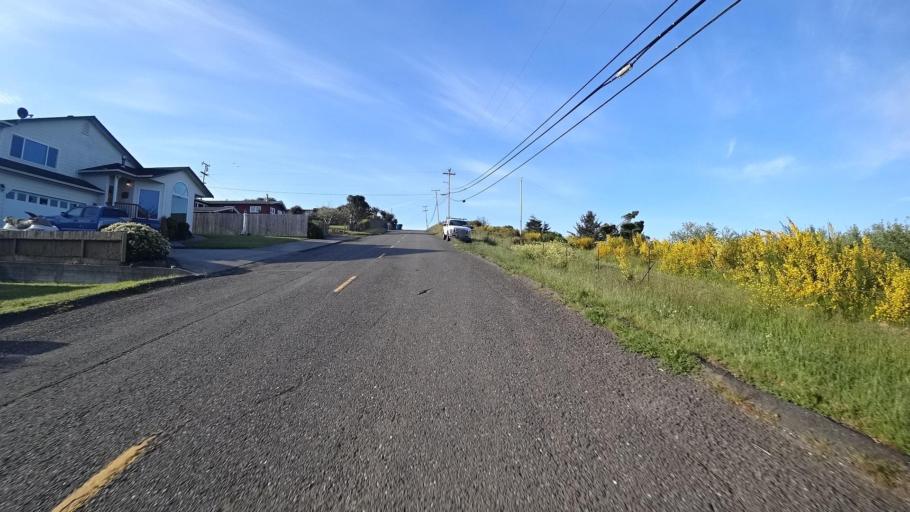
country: US
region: California
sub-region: Humboldt County
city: Humboldt Hill
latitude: 40.7314
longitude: -124.2132
